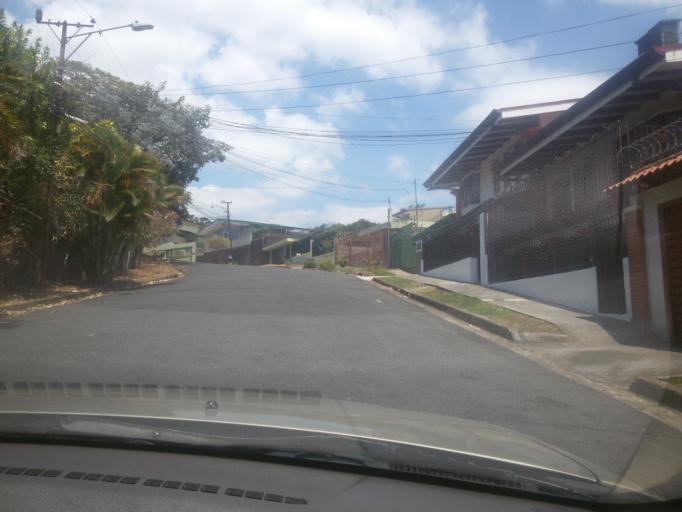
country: CR
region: San Jose
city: San Pedro
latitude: 9.9269
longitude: -84.0504
